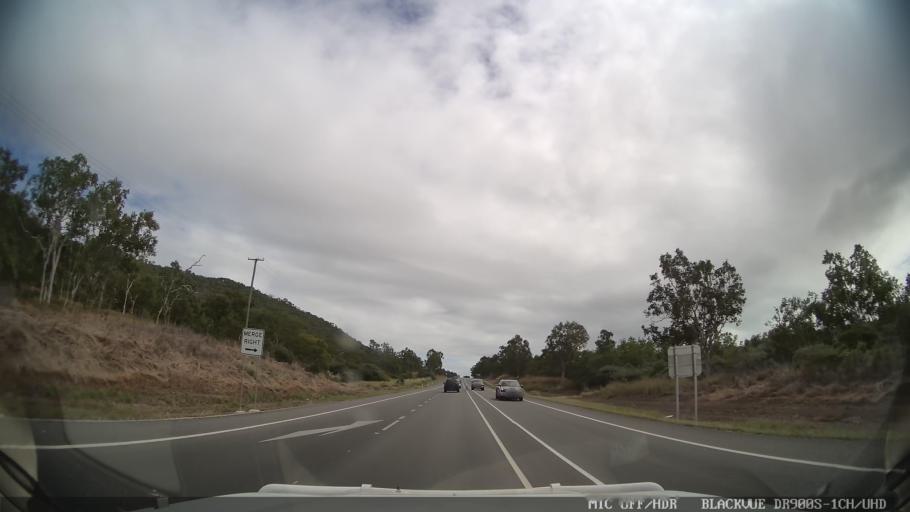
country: AU
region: Queensland
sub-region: Townsville
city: Townsville
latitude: -19.3677
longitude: 146.8930
